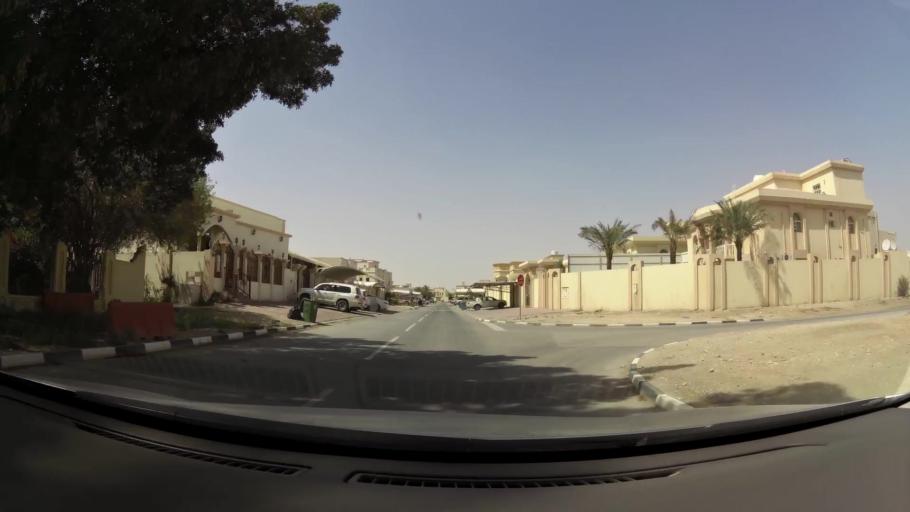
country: QA
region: Baladiyat Umm Salal
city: Umm Salal Muhammad
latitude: 25.3818
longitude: 51.4240
